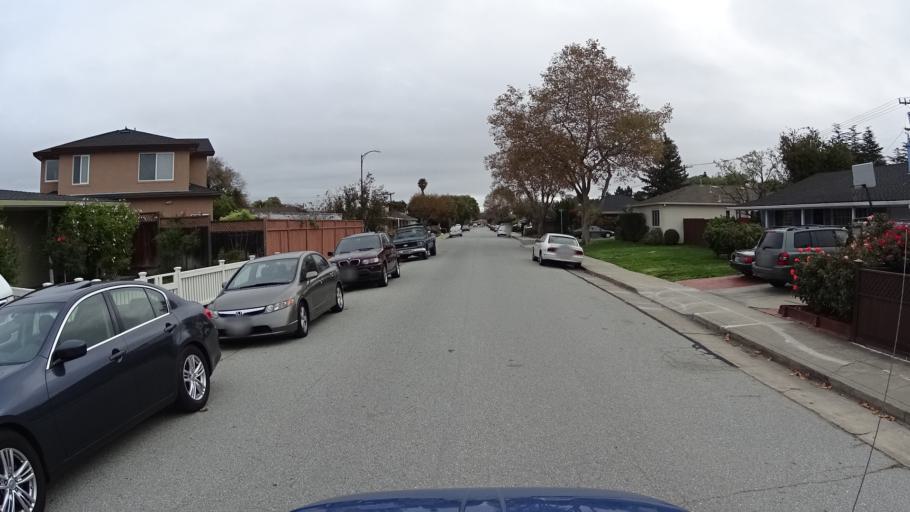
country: US
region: California
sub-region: San Mateo County
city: Belmont
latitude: 37.5342
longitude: -122.2877
